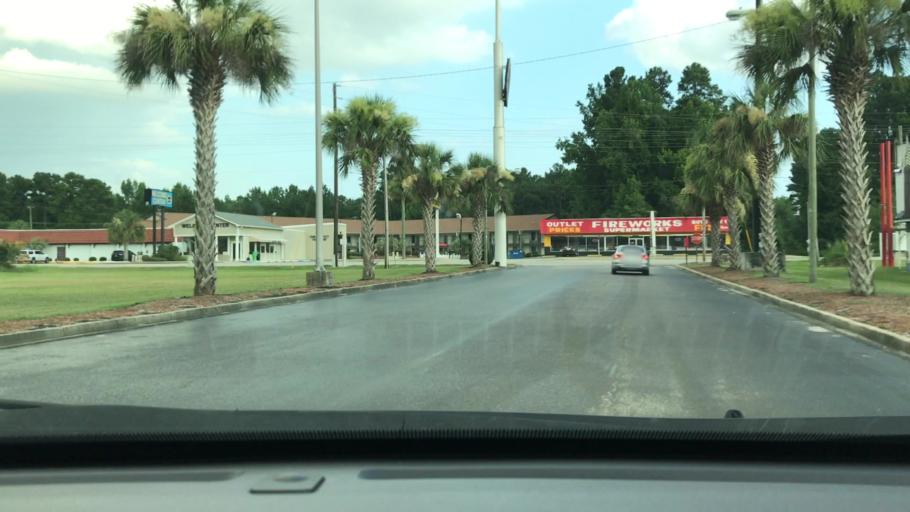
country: US
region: South Carolina
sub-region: Colleton County
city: Walterboro
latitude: 32.8805
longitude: -80.7116
